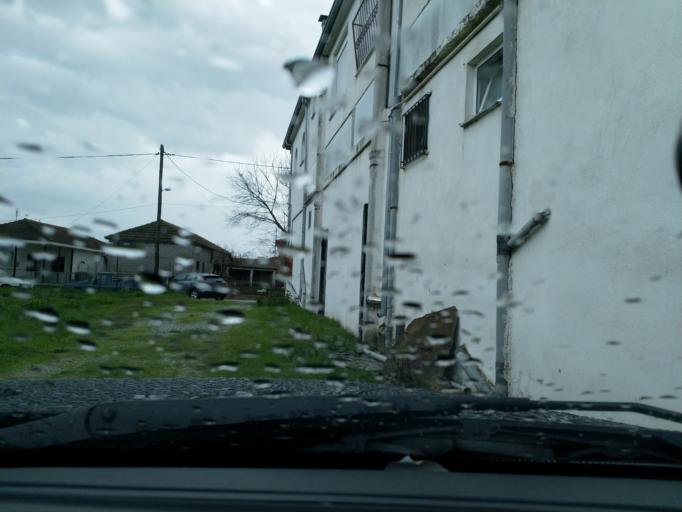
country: GR
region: Thessaly
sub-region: Trikala
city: Taxiarches
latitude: 39.5461
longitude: 21.8949
